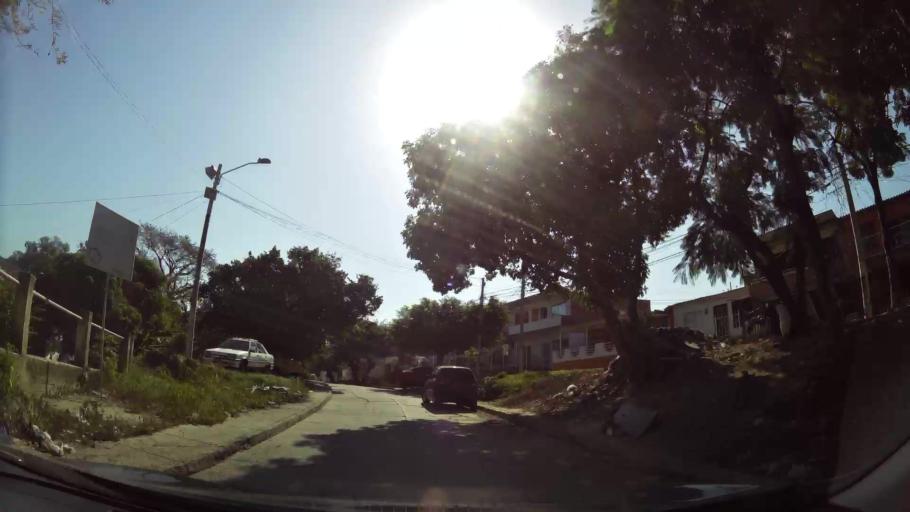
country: CO
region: Bolivar
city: Cartagena
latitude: 10.3979
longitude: -75.5157
